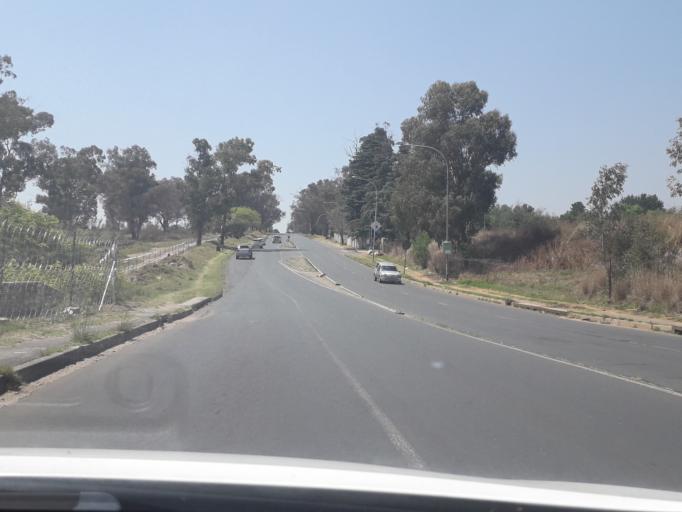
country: ZA
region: Gauteng
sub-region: City of Johannesburg Metropolitan Municipality
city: Modderfontein
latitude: -26.1402
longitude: 28.1192
